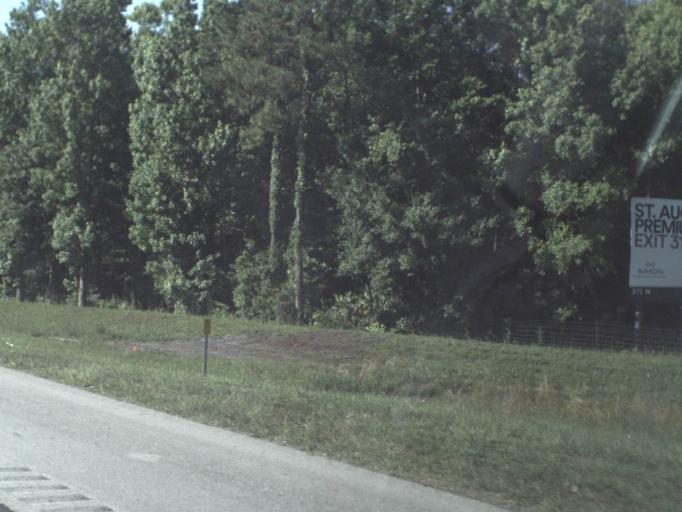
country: US
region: Florida
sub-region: Saint Johns County
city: Saint Augustine
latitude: 29.9547
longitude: -81.4429
